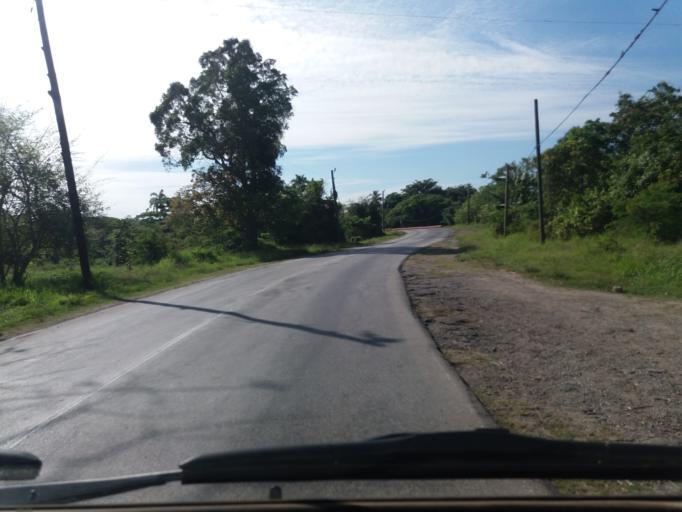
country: CU
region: Cienfuegos
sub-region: Municipio de Cienfuegos
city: Cienfuegos
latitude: 22.1644
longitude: -80.3681
